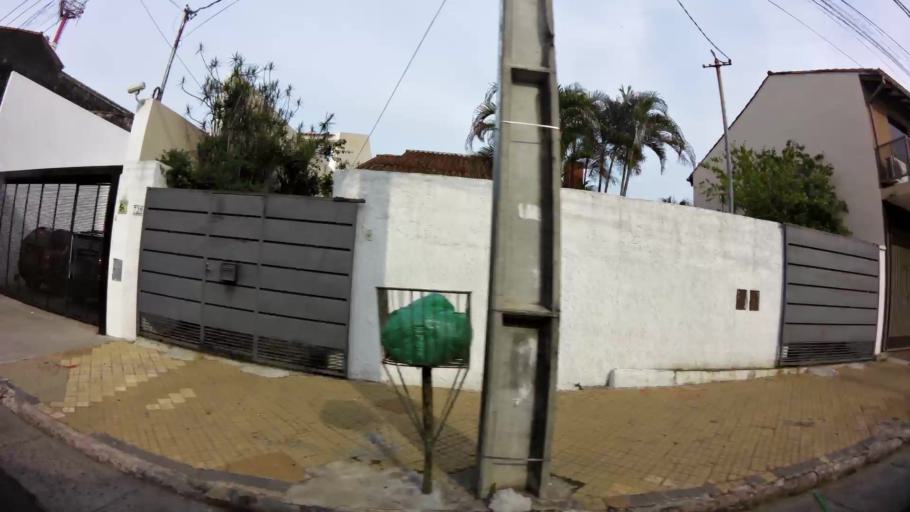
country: PY
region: Asuncion
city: Asuncion
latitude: -25.2965
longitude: -57.6166
